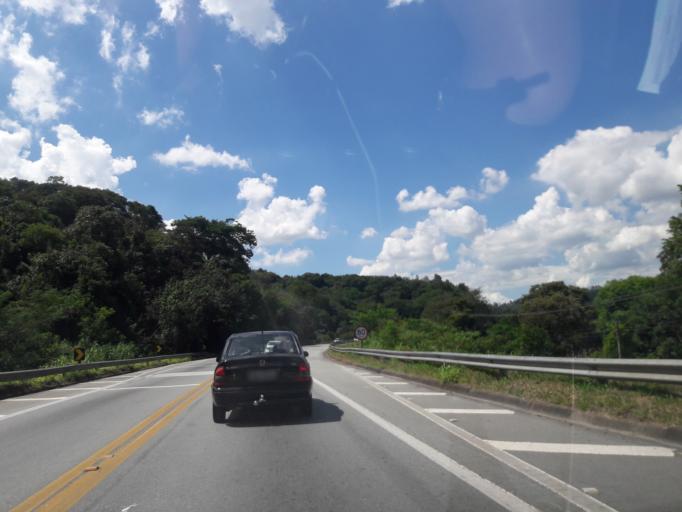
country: BR
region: Sao Paulo
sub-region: Francisco Morato
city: Francisco Morato
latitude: -23.2927
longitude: -46.8045
